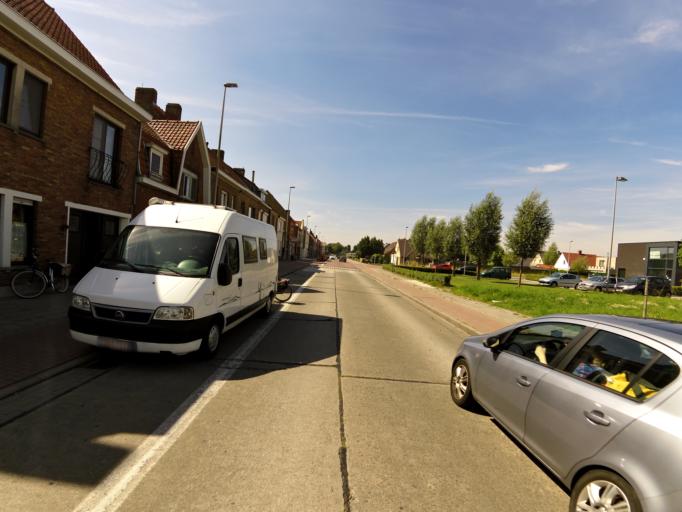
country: BE
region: Flanders
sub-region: Provincie West-Vlaanderen
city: Sint-Kruis
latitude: 51.2327
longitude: 3.2421
